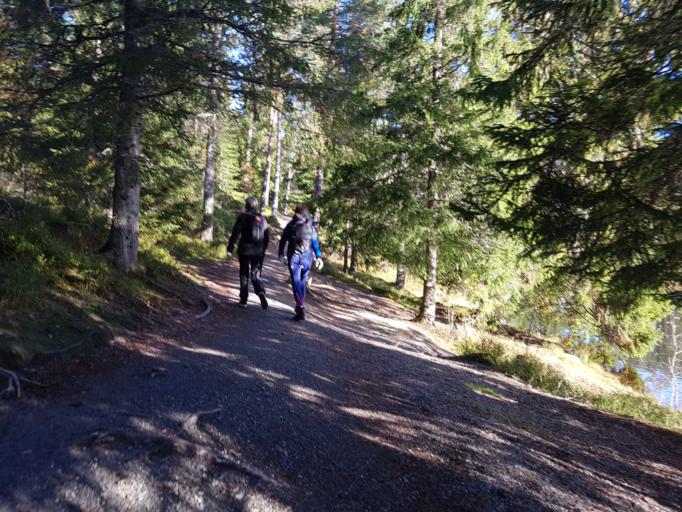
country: NO
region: Sor-Trondelag
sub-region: Trondheim
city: Trondheim
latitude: 63.4203
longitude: 10.3189
